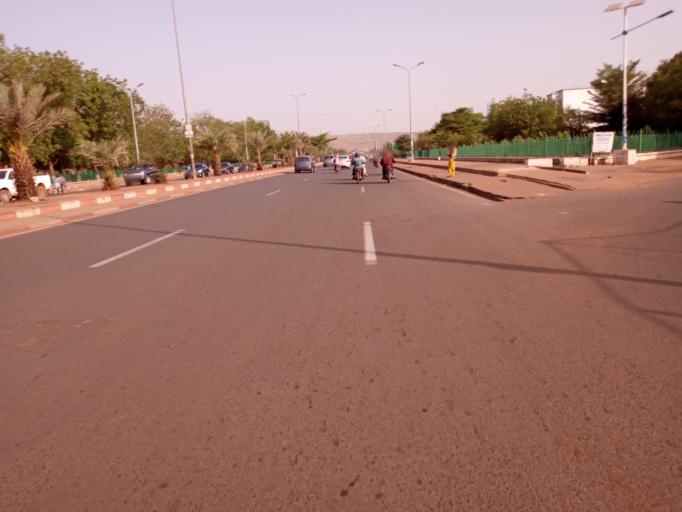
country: ML
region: Bamako
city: Bamako
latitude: 12.6390
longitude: -8.0056
